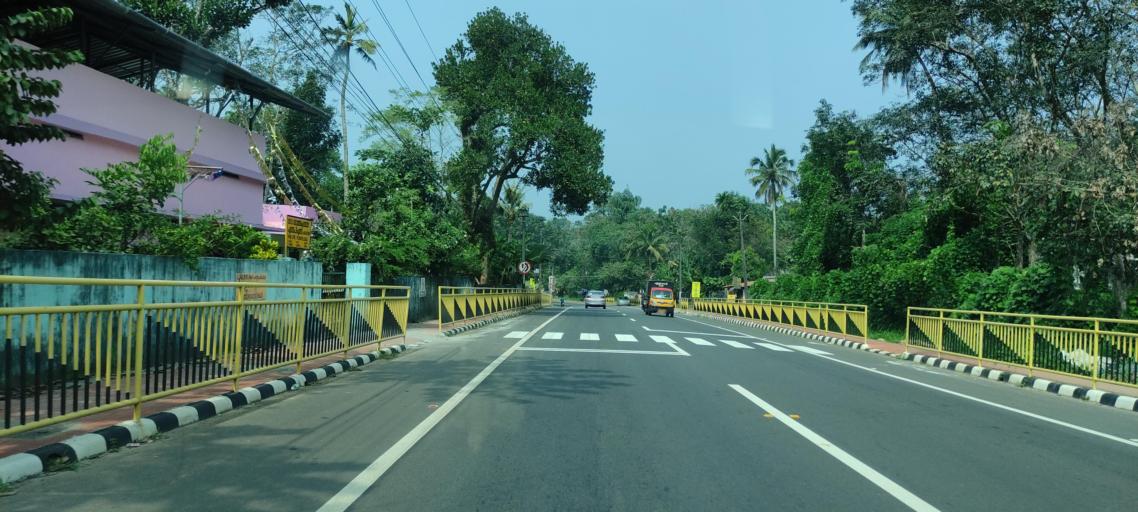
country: IN
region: Kerala
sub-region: Pattanamtitta
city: Adur
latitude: 9.1907
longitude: 76.7054
